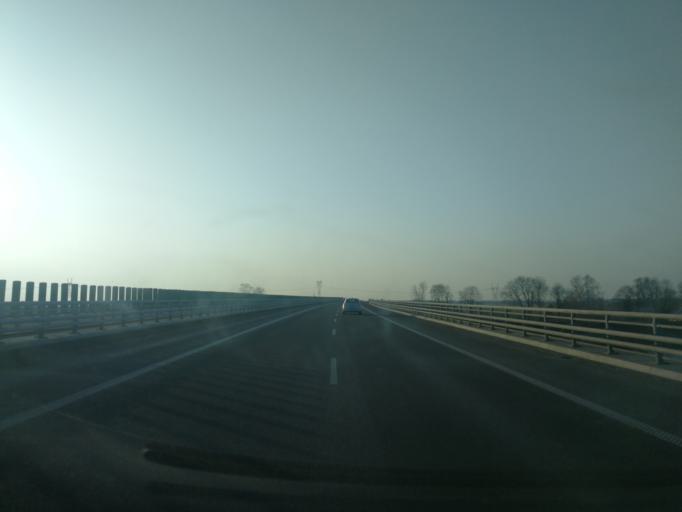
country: PL
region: Warmian-Masurian Voivodeship
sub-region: Powiat elblaski
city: Gronowo Elblaskie
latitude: 54.1655
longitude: 19.2431
